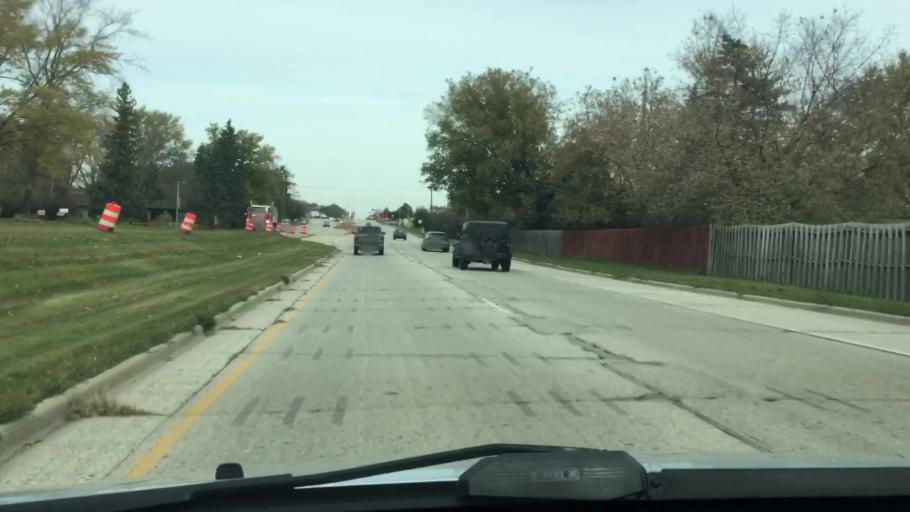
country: US
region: Wisconsin
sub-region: Waukesha County
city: New Berlin
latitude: 42.9715
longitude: -88.1085
